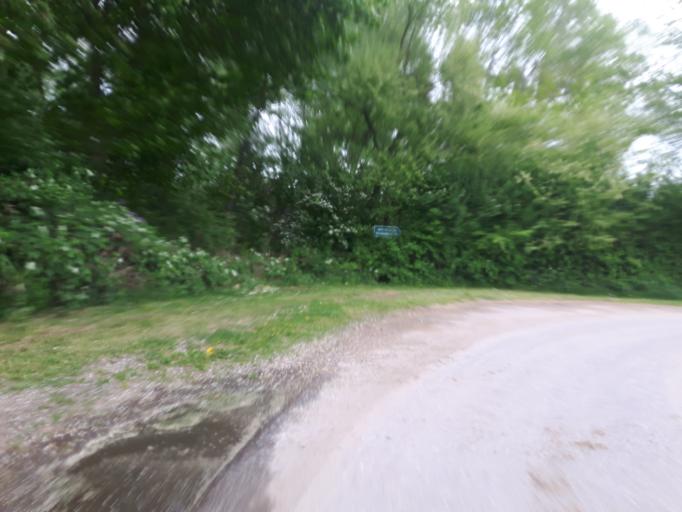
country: DE
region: Baden-Wuerttemberg
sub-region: Karlsruhe Region
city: Sankt Leon-Rot
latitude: 49.2777
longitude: 8.5984
